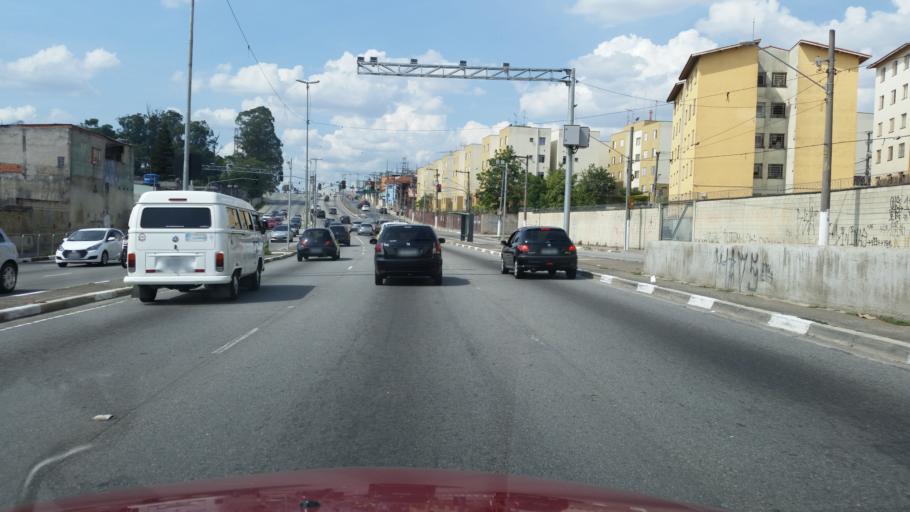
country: BR
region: Sao Paulo
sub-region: Ferraz De Vasconcelos
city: Ferraz de Vasconcelos
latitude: -23.5308
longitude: -46.4484
